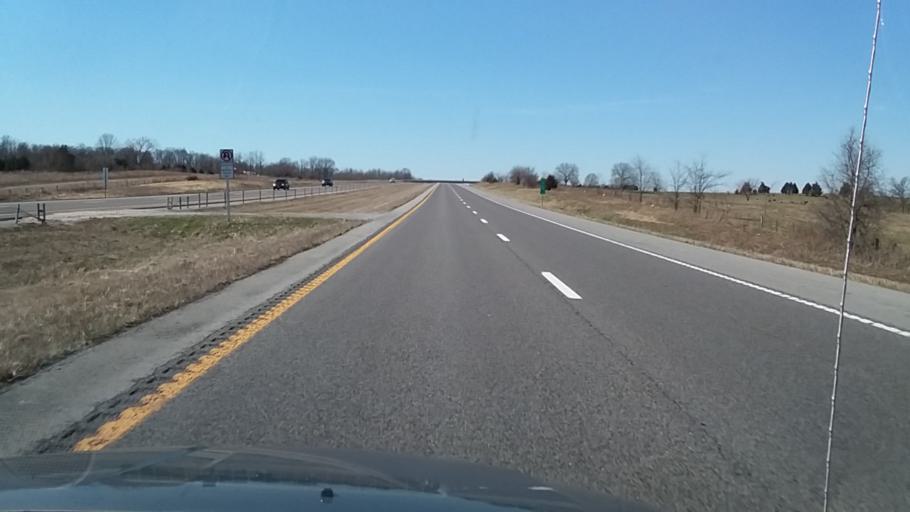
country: US
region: Missouri
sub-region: Cape Girardeau County
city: Jackson
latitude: 37.5445
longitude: -89.7282
